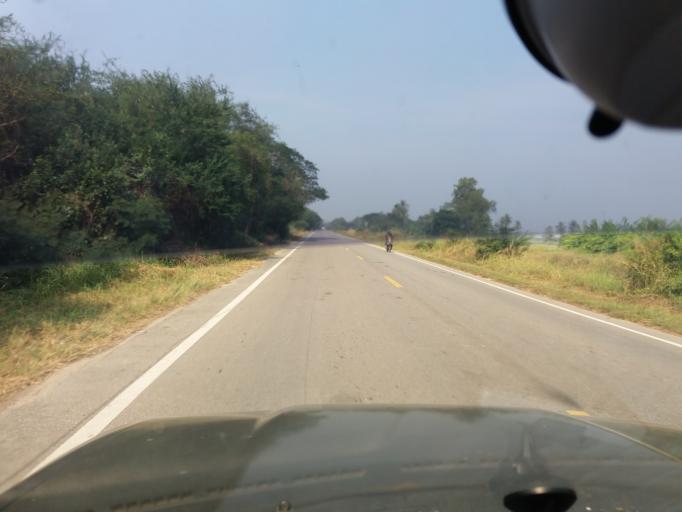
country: TH
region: Sing Buri
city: Bang Racham
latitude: 14.9065
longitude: 100.2621
